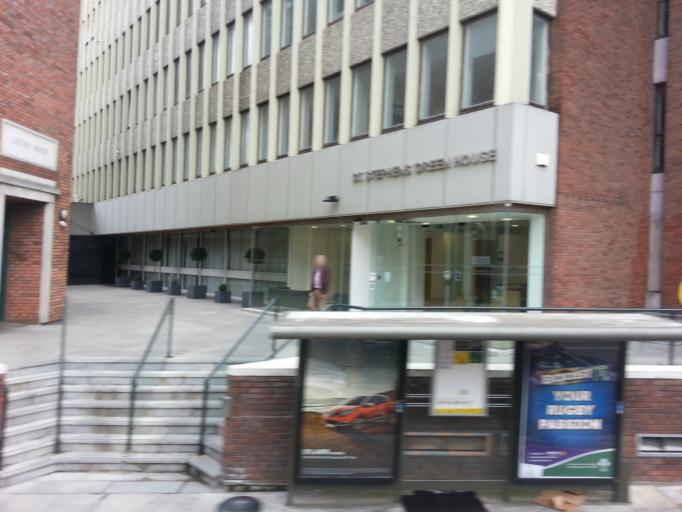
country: IE
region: Leinster
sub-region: Dublin City
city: Dublin
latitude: 53.3355
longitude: -6.2576
